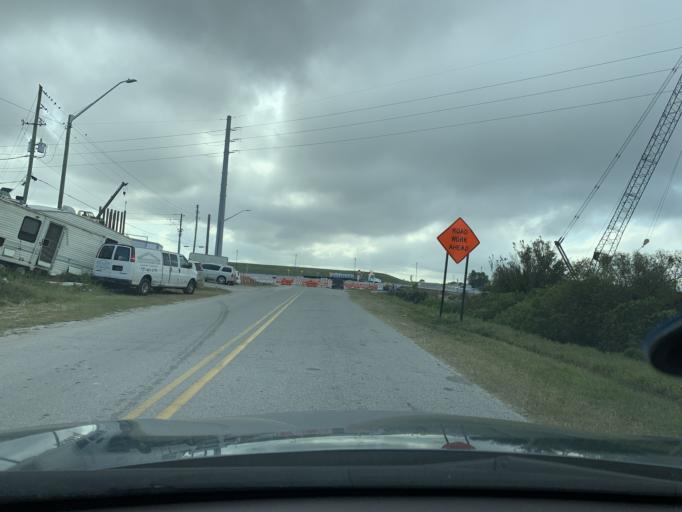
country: US
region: Florida
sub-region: Pinellas County
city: Pinellas Park
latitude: 27.8803
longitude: -82.6880
